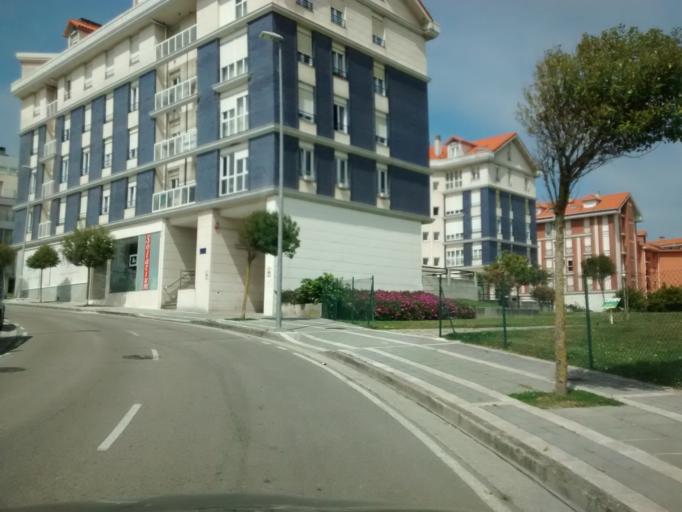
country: ES
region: Cantabria
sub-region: Provincia de Cantabria
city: Santander
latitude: 43.4811
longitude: -3.7981
